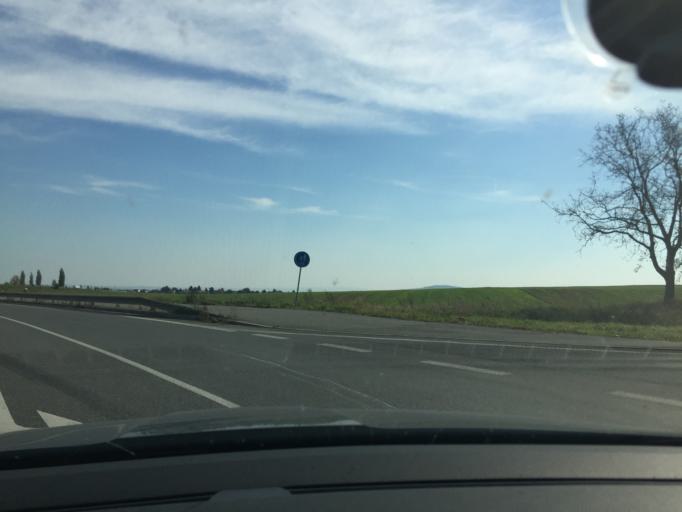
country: CZ
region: Central Bohemia
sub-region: Okres Kolin
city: Kolin
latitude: 50.0109
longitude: 15.1908
